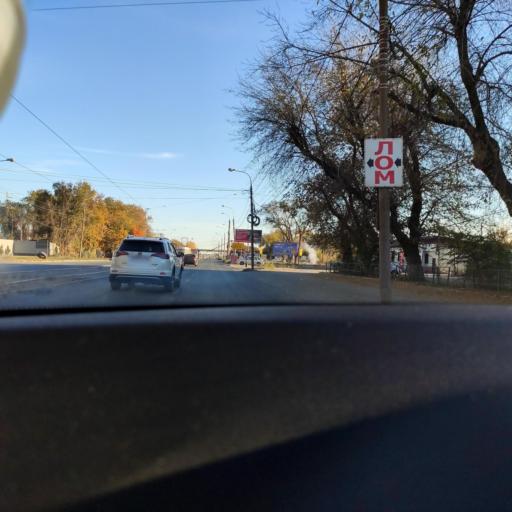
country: RU
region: Samara
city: Smyshlyayevka
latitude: 53.1944
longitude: 50.2918
